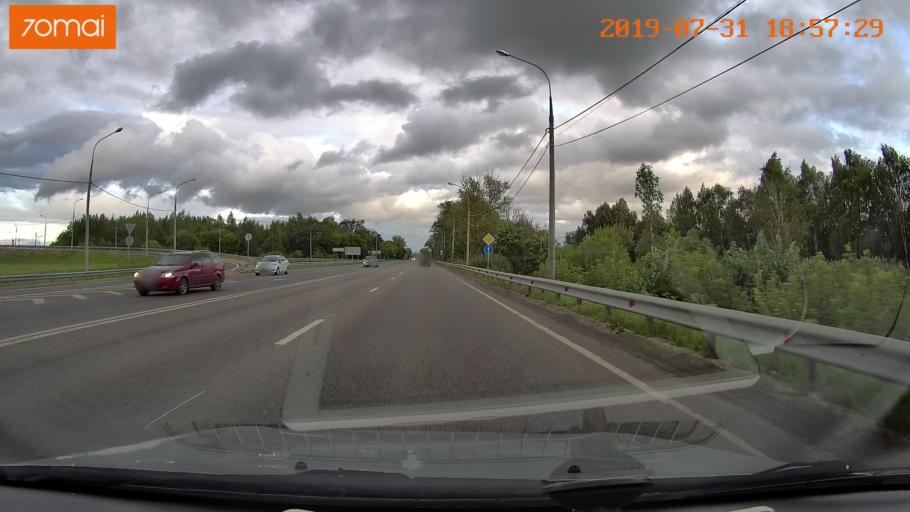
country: RU
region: Moskovskaya
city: Raduzhnyy
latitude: 55.1537
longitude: 38.6928
